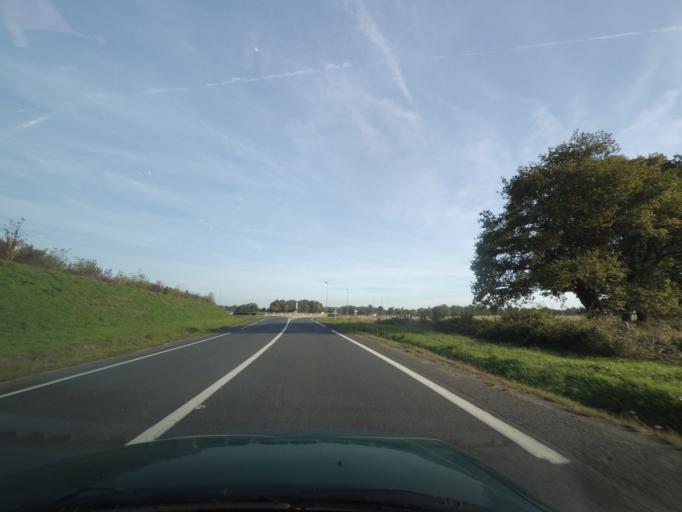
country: FR
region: Pays de la Loire
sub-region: Departement de la Vendee
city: Montaigu
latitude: 46.9795
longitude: -1.2895
